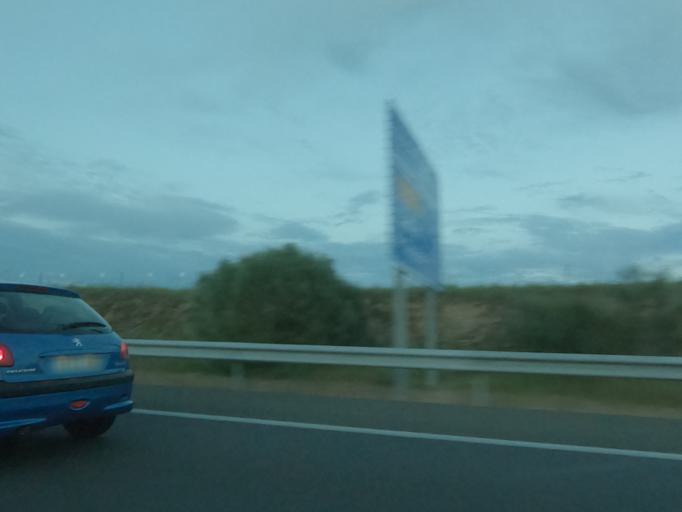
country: ES
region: Extremadura
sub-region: Provincia de Caceres
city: Casar de Caceres
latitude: 39.5431
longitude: -6.4040
